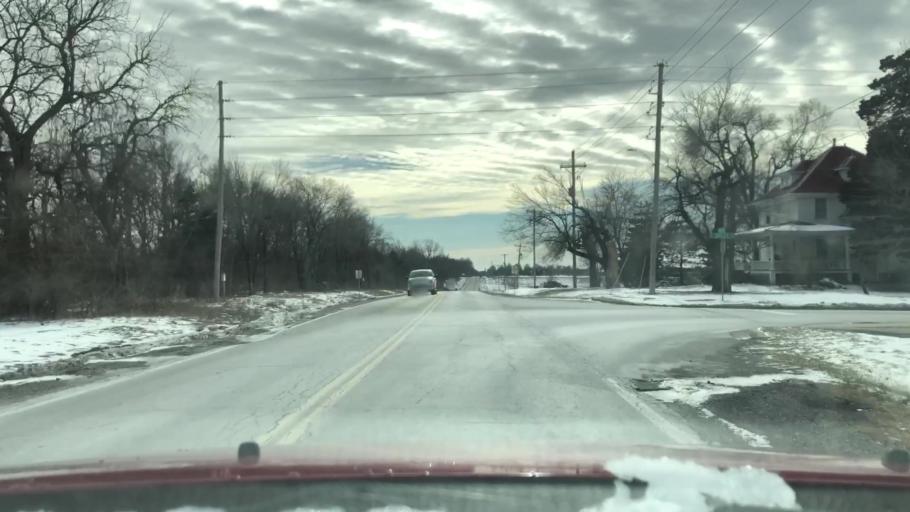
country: US
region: Missouri
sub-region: Jackson County
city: Greenwood
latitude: 38.8953
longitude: -94.3402
